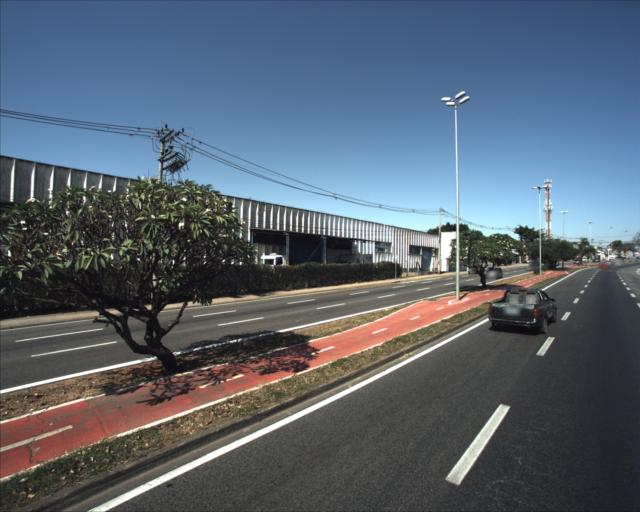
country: BR
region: Sao Paulo
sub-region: Sorocaba
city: Sorocaba
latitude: -23.4476
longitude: -47.4797
